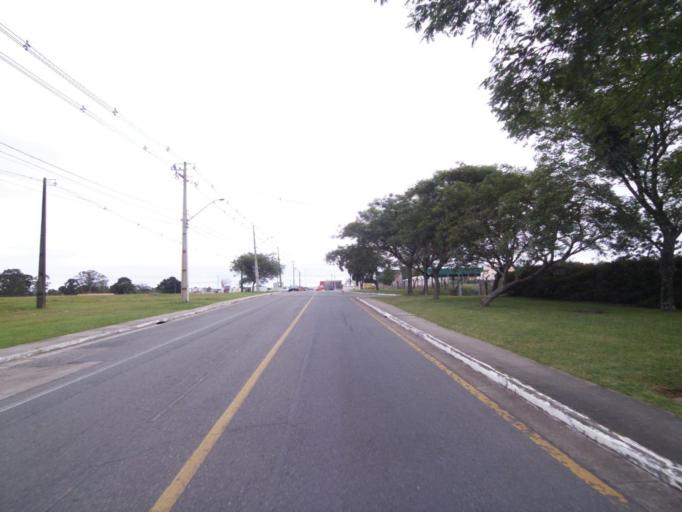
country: BR
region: Parana
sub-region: Sao Jose Dos Pinhais
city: Sao Jose dos Pinhais
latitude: -25.5347
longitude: -49.1794
